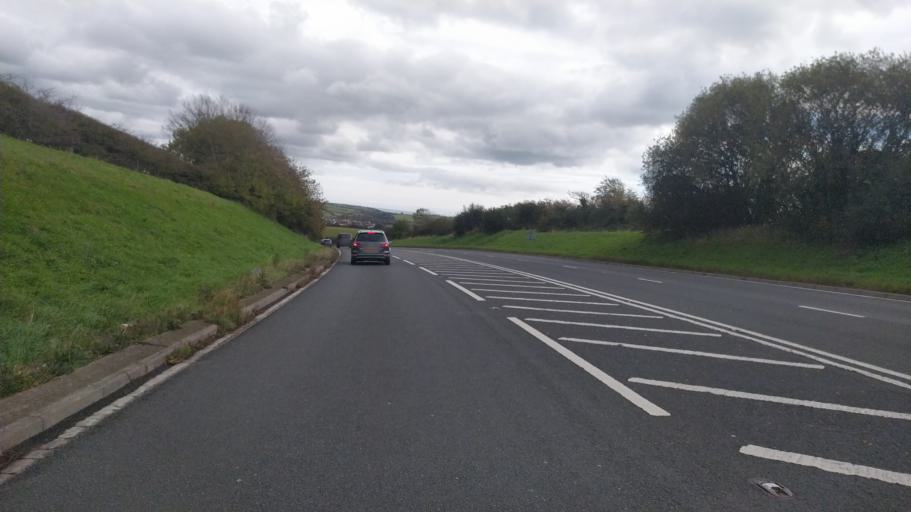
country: GB
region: England
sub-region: Dorset
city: Bridport
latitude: 50.7245
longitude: -2.7752
